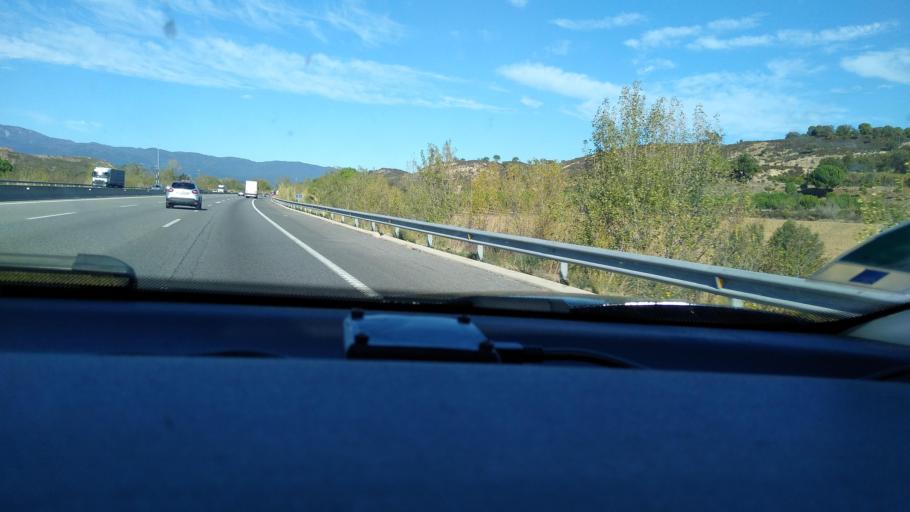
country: ES
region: Catalonia
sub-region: Provincia de Girona
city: Pont de Molins
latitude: 42.3384
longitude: 2.9233
